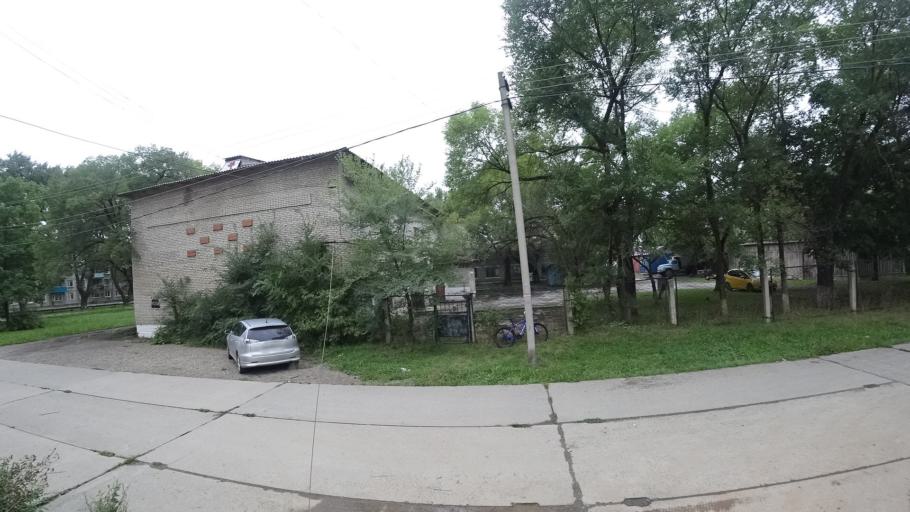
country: RU
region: Primorskiy
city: Chernigovka
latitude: 44.3328
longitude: 132.5373
